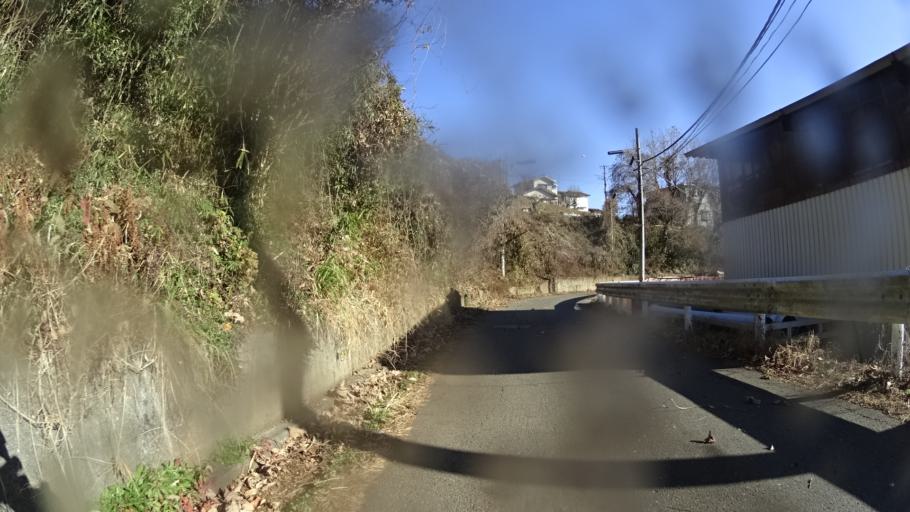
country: JP
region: Yamanashi
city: Uenohara
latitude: 35.6165
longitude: 139.1648
